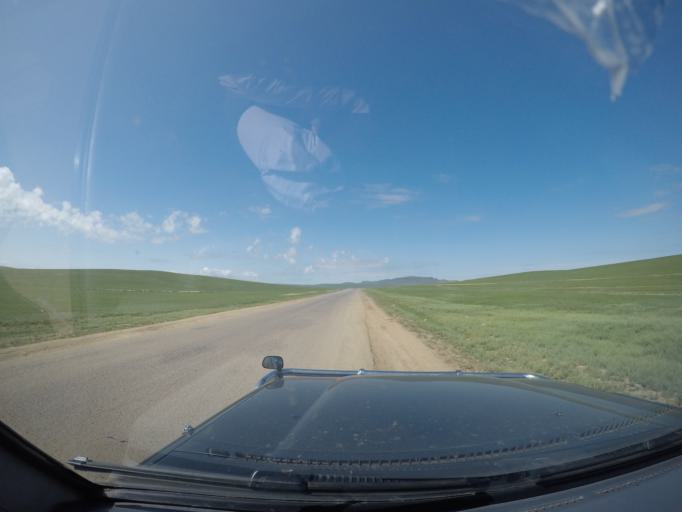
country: MN
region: Hentiy
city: Dundburd
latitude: 47.3450
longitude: 111.5173
